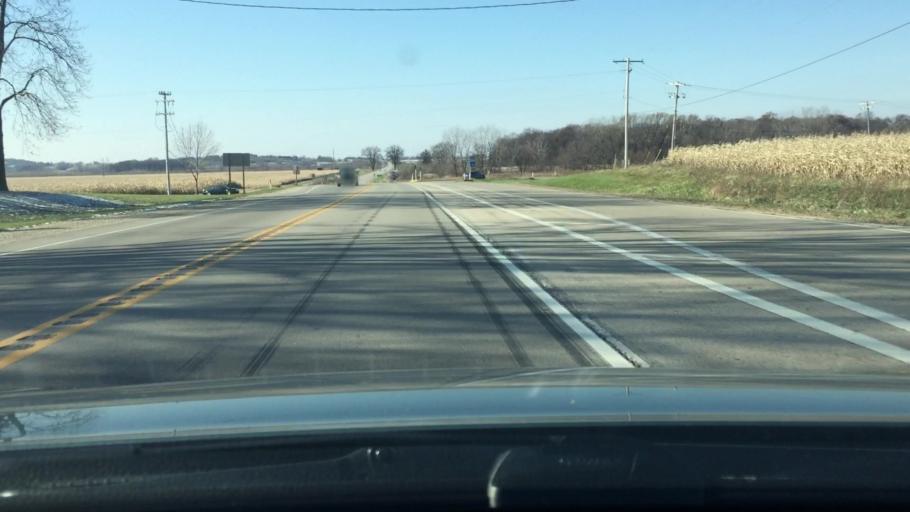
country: US
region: Wisconsin
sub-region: Jefferson County
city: Jefferson
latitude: 43.0070
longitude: -88.8534
